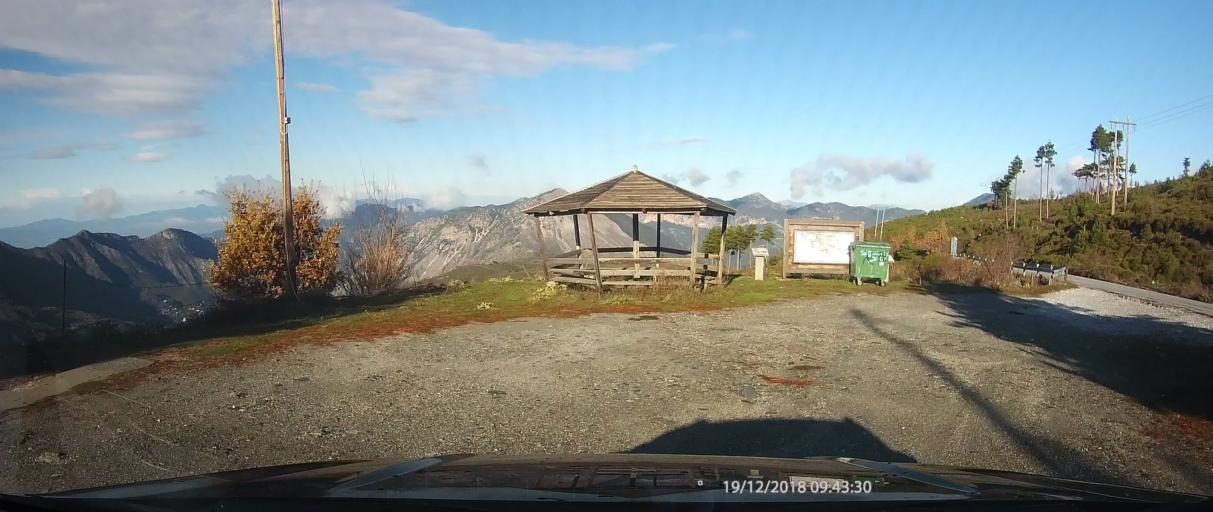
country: GR
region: Peloponnese
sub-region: Nomos Messinias
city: Paralia Vergas
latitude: 37.0714
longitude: 22.2571
